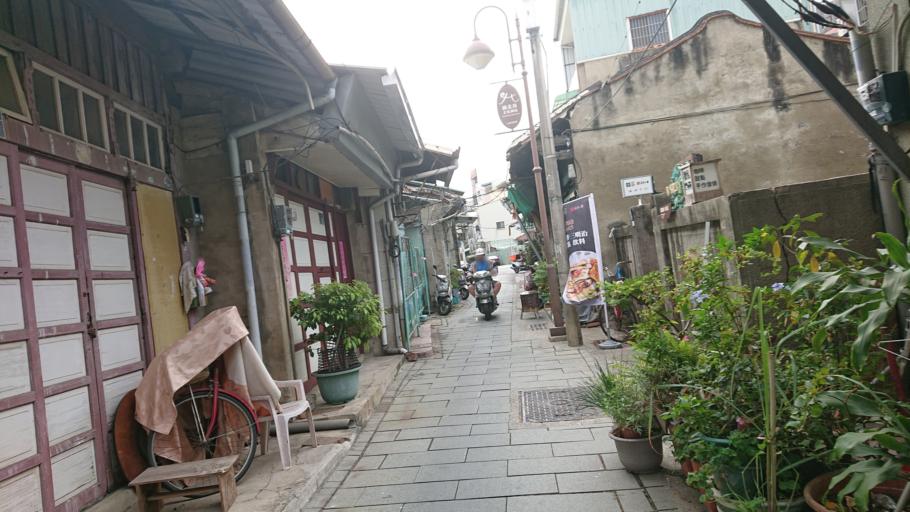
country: TW
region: Taiwan
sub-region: Tainan
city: Tainan
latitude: 23.0006
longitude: 120.2028
